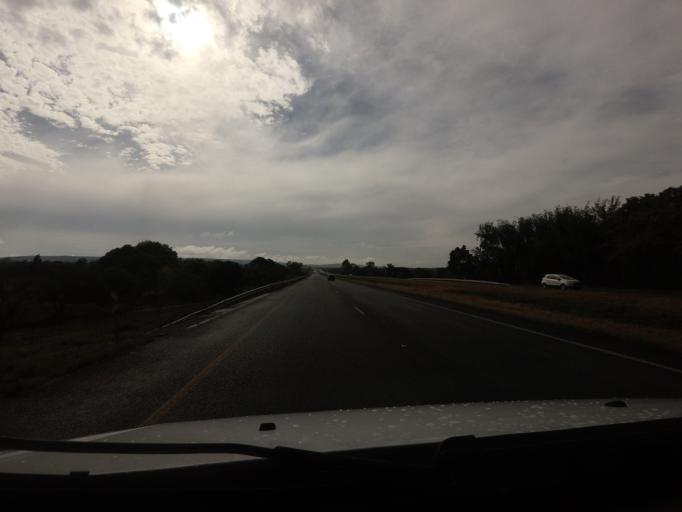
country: ZA
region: Gauteng
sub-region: City of Tshwane Metropolitan Municipality
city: Cullinan
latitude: -25.7669
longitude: 28.3985
